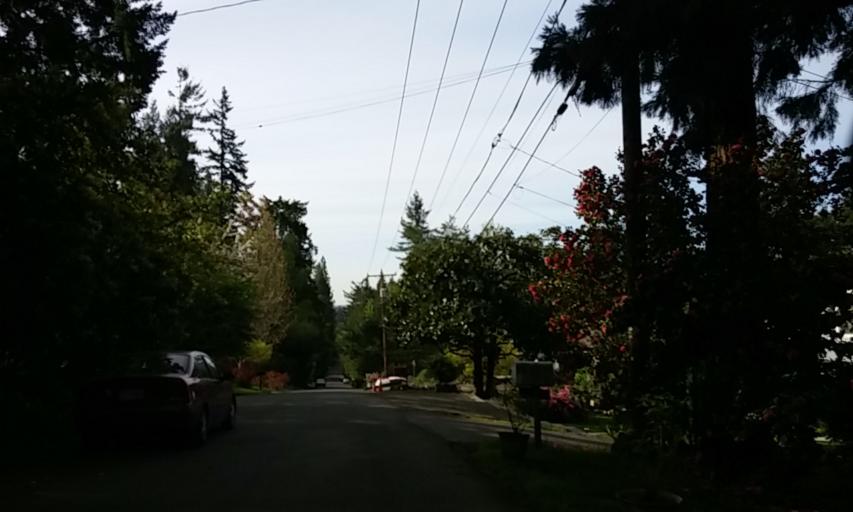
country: US
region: Oregon
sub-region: Washington County
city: West Slope
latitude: 45.5032
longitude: -122.7667
